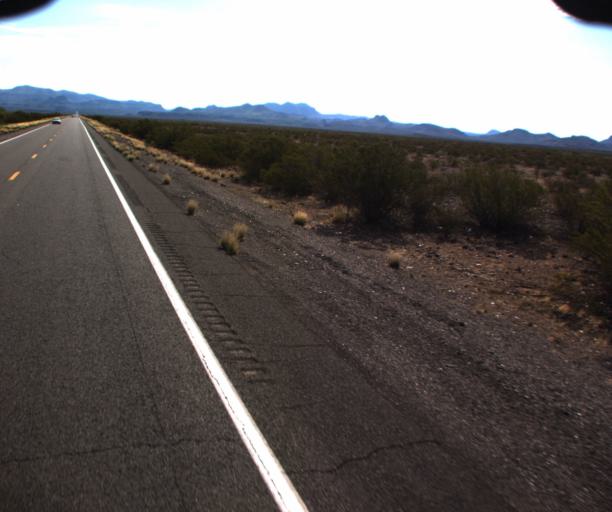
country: US
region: Arizona
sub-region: Graham County
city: Safford
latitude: 32.8121
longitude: -109.4982
